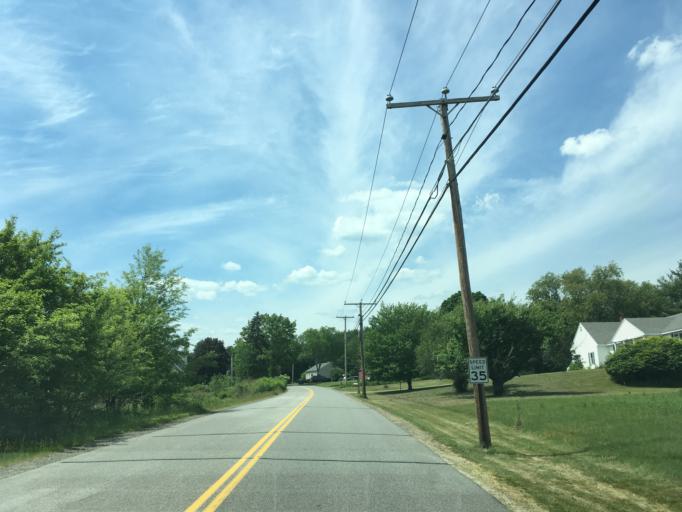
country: US
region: New Hampshire
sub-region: Rockingham County
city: Stratham Station
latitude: 43.0317
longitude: -70.8724
